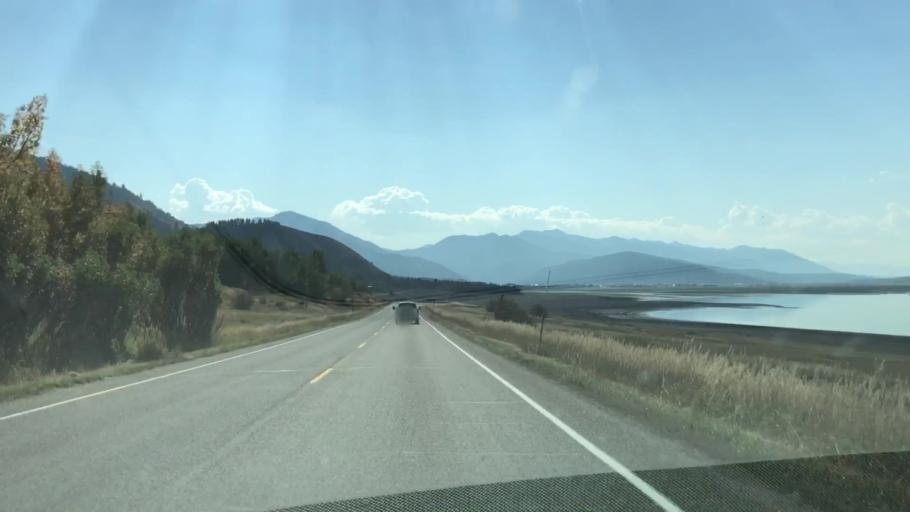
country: US
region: Wyoming
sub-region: Teton County
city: Hoback
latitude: 43.2220
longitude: -111.0746
